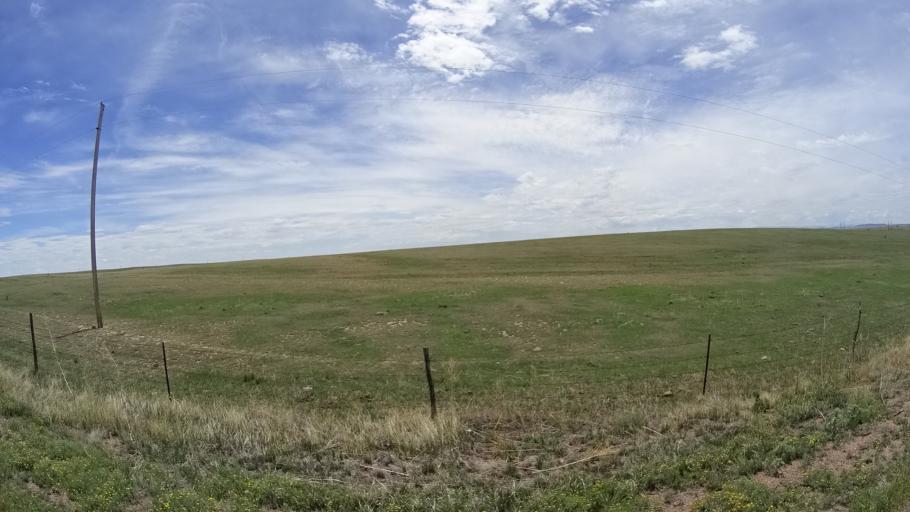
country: US
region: Colorado
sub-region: El Paso County
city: Fountain
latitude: 38.6940
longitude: -104.6117
